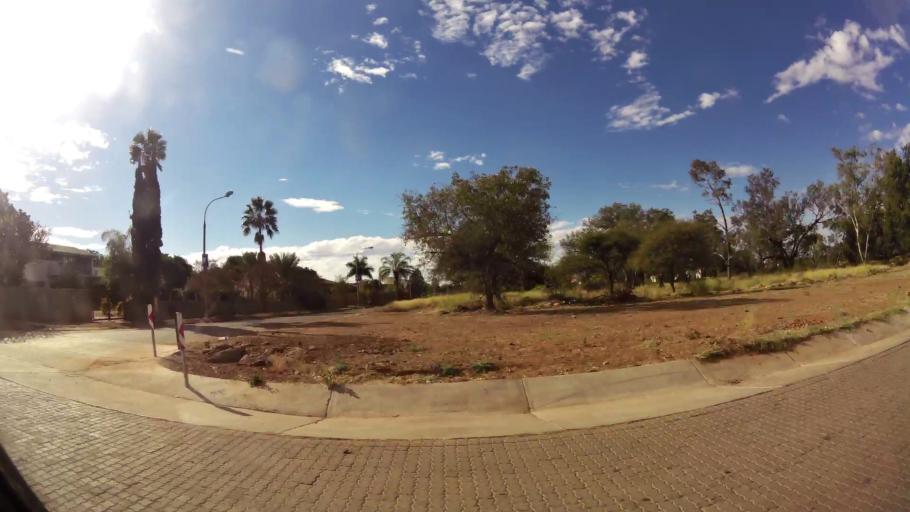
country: ZA
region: Limpopo
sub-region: Waterberg District Municipality
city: Warmbaths
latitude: -24.8797
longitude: 28.2731
